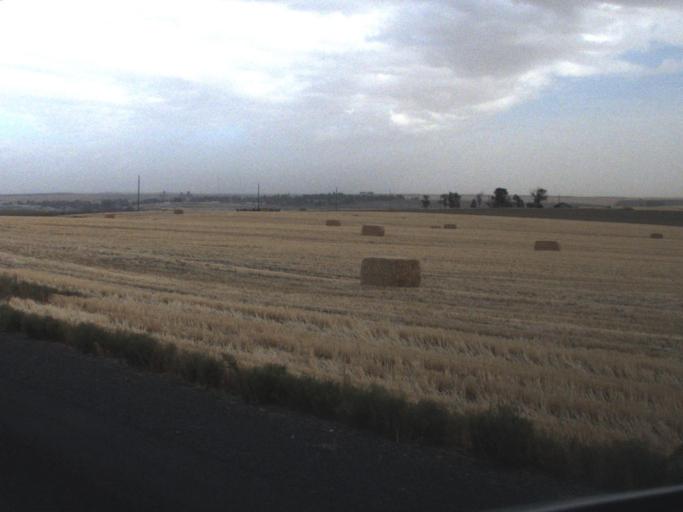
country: US
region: Washington
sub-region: Lincoln County
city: Davenport
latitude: 47.4634
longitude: -118.3020
